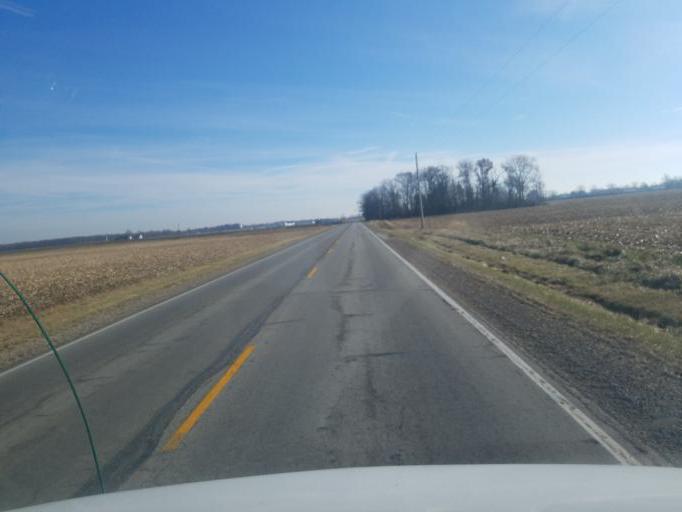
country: US
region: Indiana
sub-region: Adams County
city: Geneva
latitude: 40.5409
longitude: -84.9754
